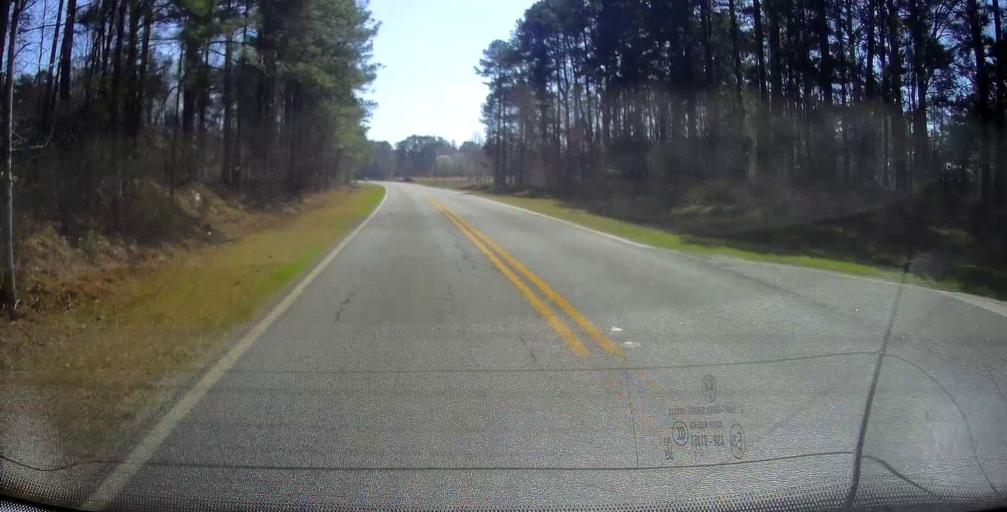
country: US
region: Georgia
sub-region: Jones County
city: Gray
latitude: 32.9716
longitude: -83.5481
